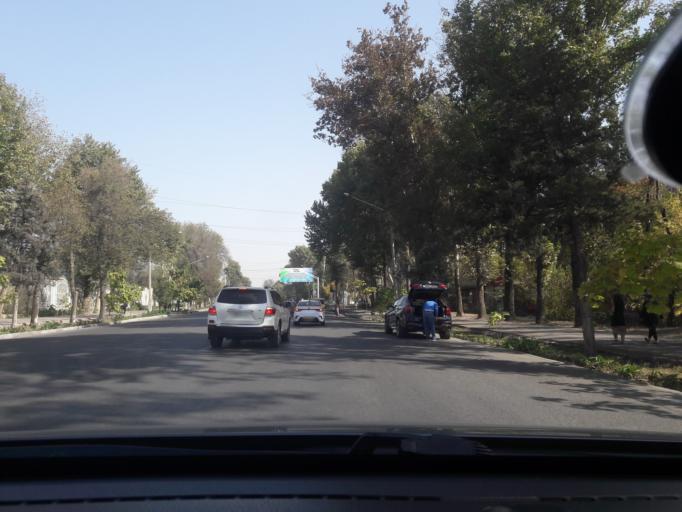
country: TJ
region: Dushanbe
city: Dushanbe
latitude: 38.5179
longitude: 68.7530
